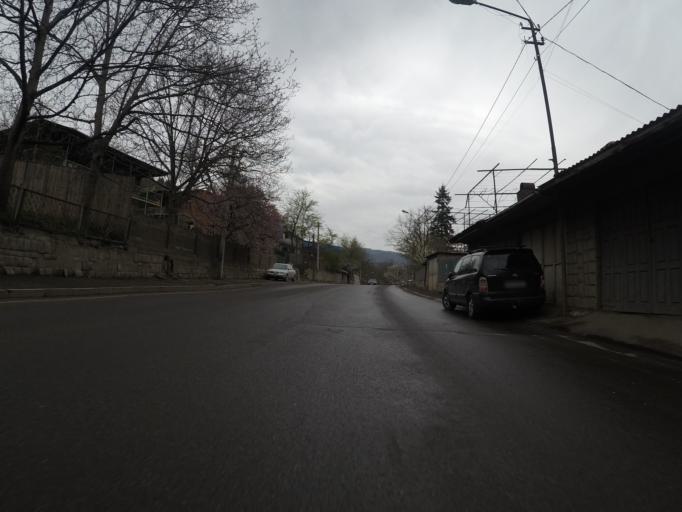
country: GE
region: Samtskhe-Javakheti
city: Borjomi
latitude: 41.8513
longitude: 43.4129
